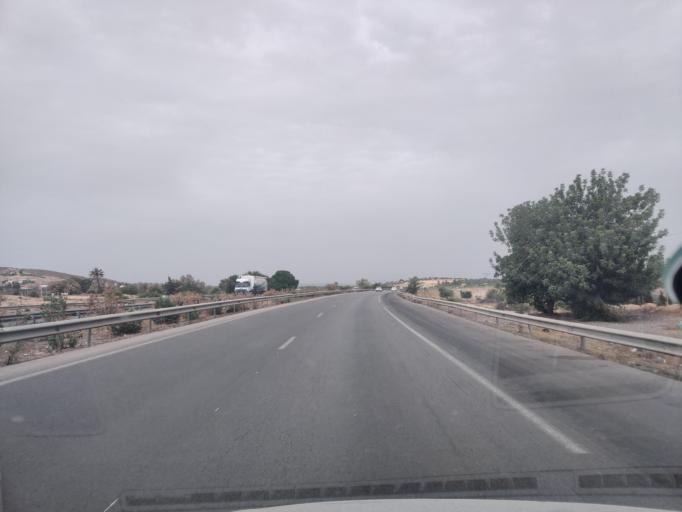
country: TN
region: Susah
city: Harqalah
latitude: 36.2323
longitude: 10.4139
